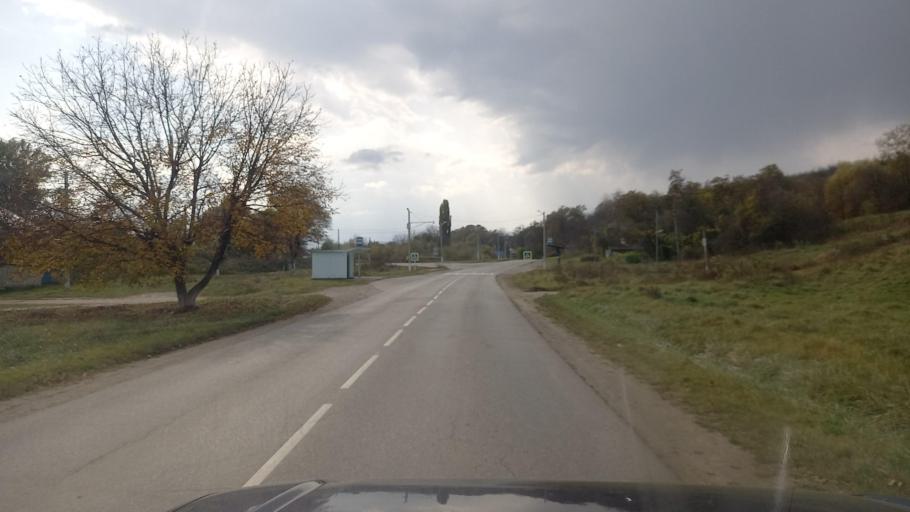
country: RU
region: Krasnodarskiy
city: Psebay
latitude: 44.1323
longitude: 40.8124
